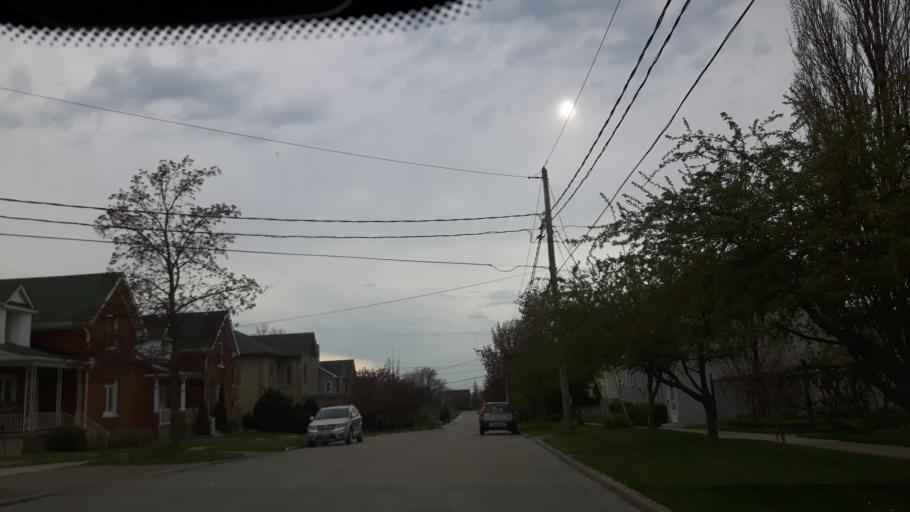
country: CA
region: Ontario
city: Goderich
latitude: 43.7440
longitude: -81.7129
